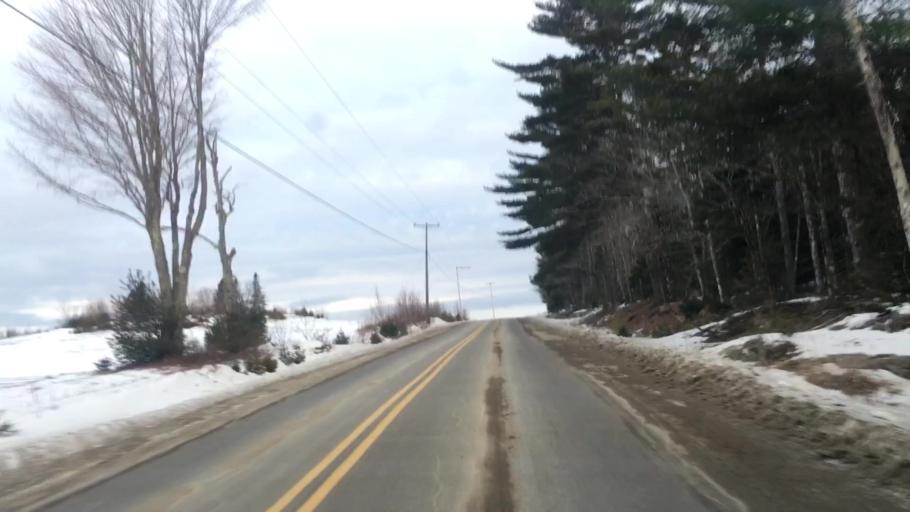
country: US
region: Maine
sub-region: Hancock County
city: Franklin
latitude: 44.8433
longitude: -68.3263
